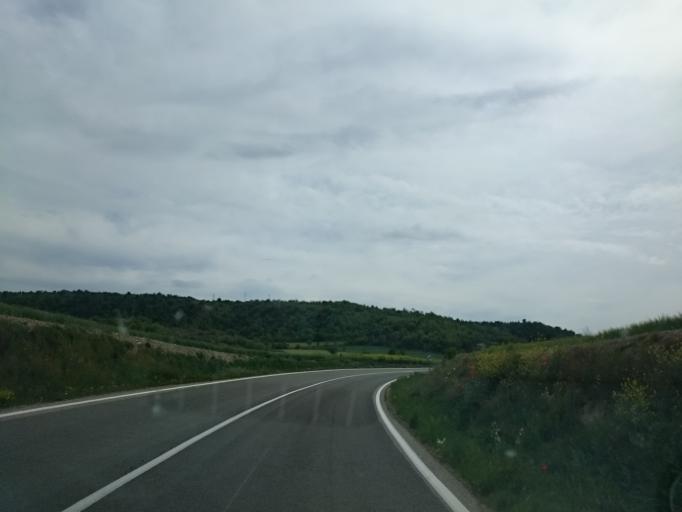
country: ES
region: Catalonia
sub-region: Provincia de Lleida
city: Tora de Riubregos
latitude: 41.7954
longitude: 1.4015
